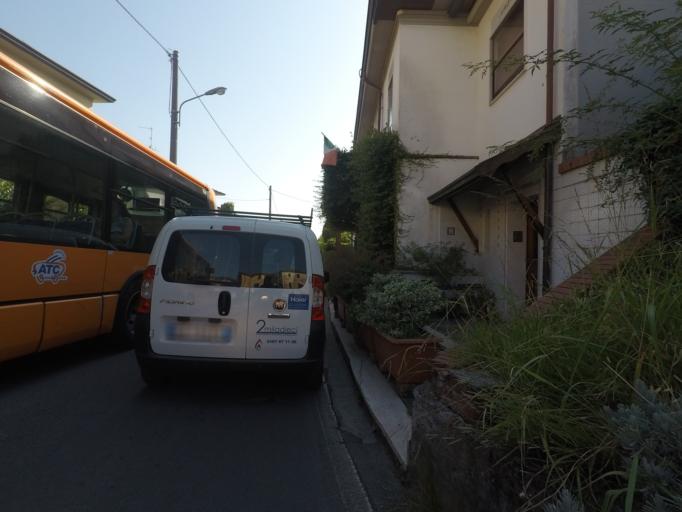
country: IT
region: Liguria
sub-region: Provincia di La Spezia
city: Casano-Dogana-Isola
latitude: 44.0809
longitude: 10.0343
